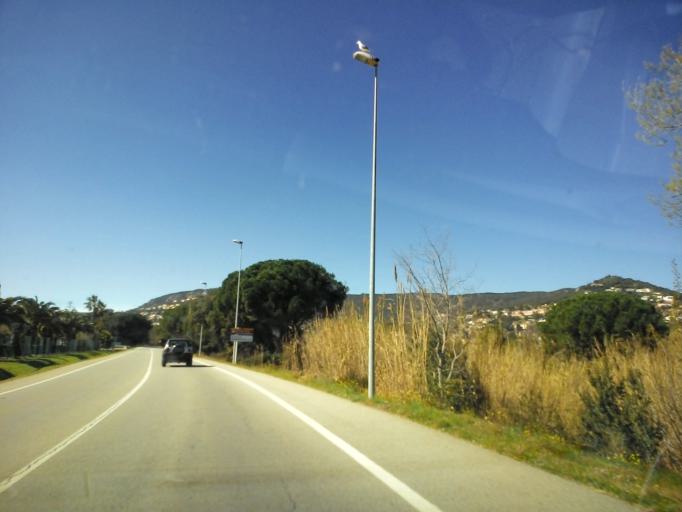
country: ES
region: Catalonia
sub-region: Provincia de Girona
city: Calonge
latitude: 41.8580
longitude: 3.0765
